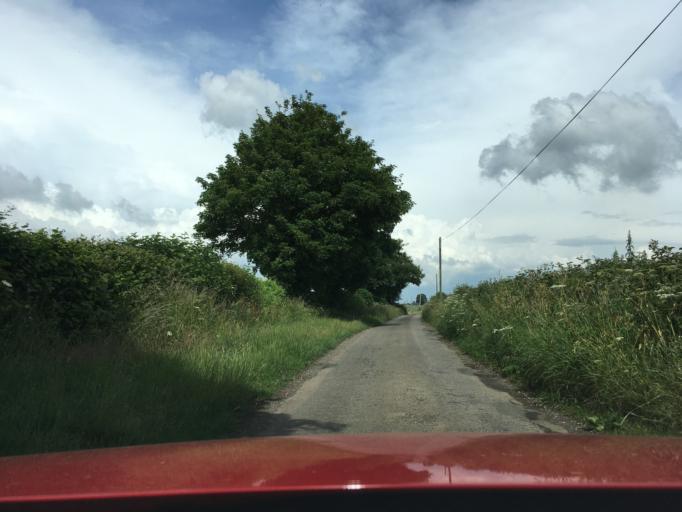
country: GB
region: England
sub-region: Gloucestershire
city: Tetbury
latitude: 51.6656
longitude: -2.1730
